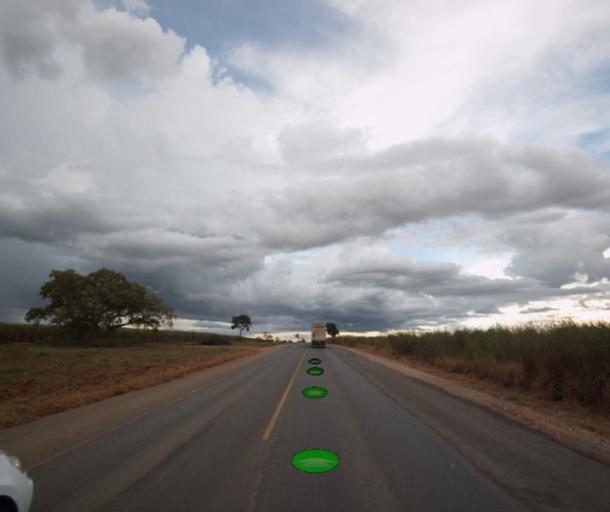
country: BR
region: Goias
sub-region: Itapaci
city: Itapaci
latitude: -14.8022
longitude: -49.2860
